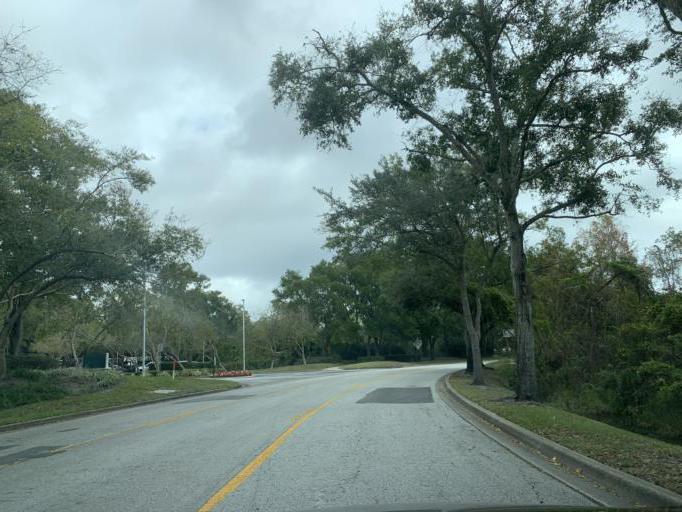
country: US
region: Florida
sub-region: Orange County
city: Eatonville
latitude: 28.6279
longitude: -81.3964
